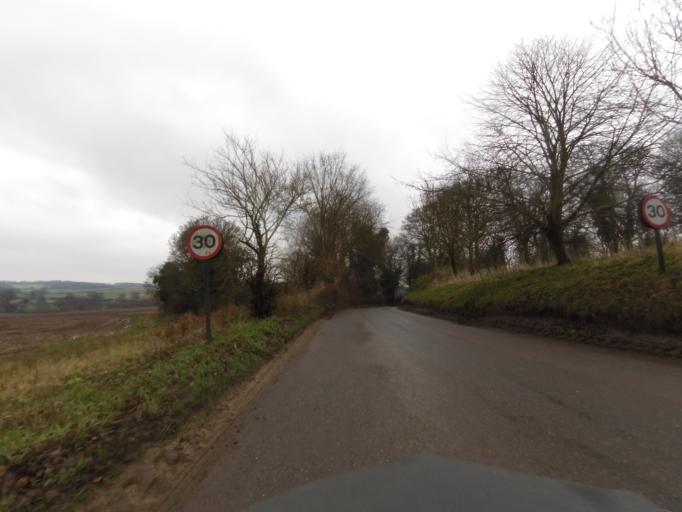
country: GB
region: England
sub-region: Norfolk
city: Briston
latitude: 52.8787
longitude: 1.0778
